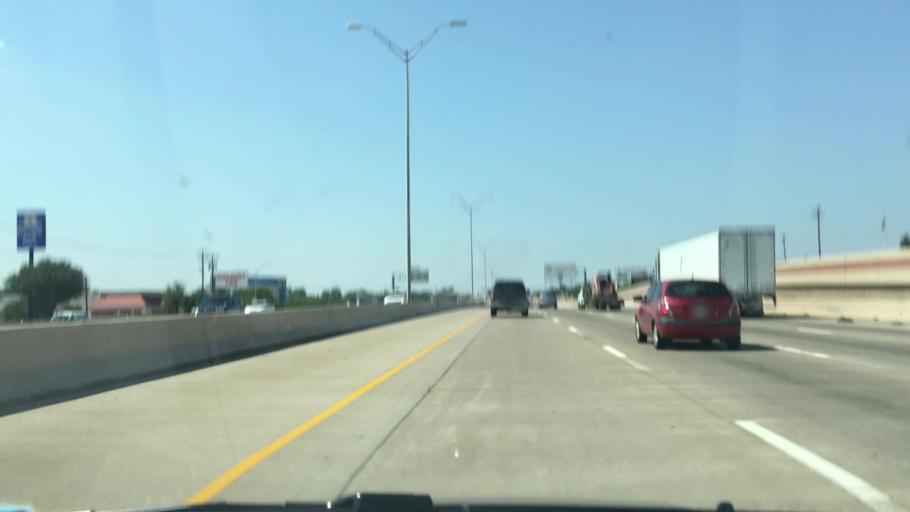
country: US
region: Texas
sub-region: Dallas County
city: DeSoto
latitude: 32.6088
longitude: -96.8229
